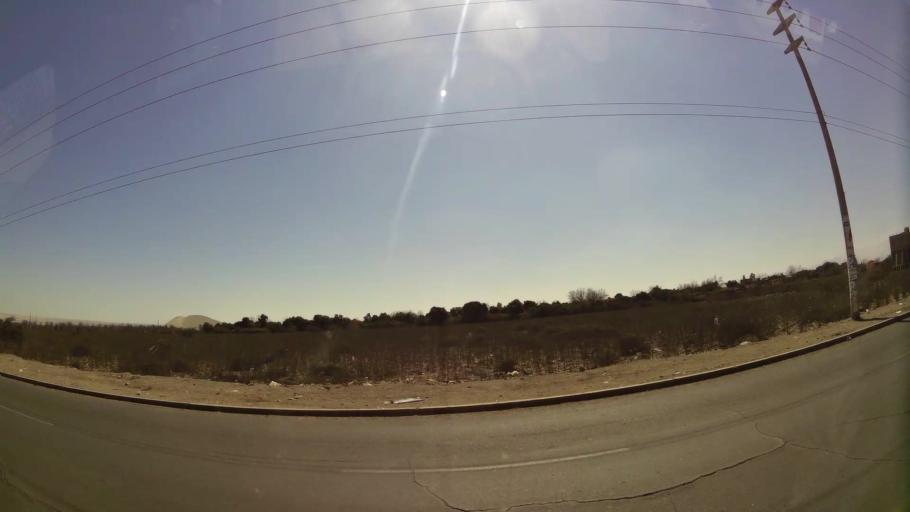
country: PE
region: Ica
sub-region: Provincia de Ica
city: La Tinguina
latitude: -14.0557
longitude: -75.7080
